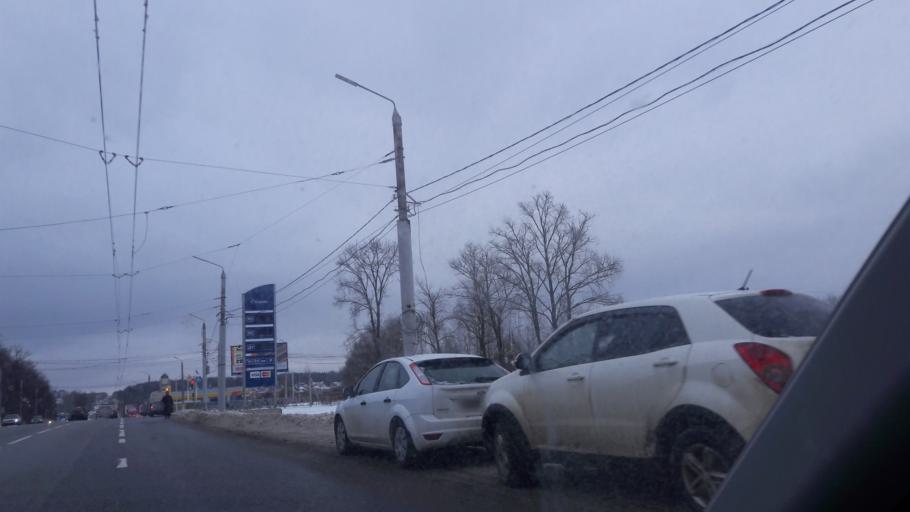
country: RU
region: Tula
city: Gorelki
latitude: 54.2404
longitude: 37.6192
